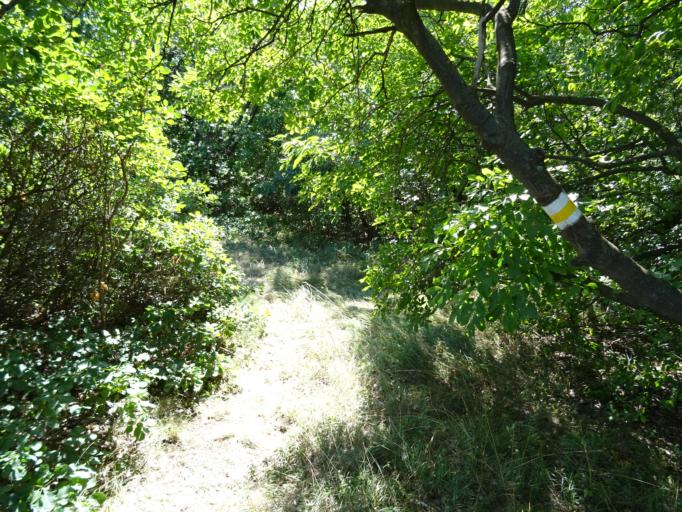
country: HU
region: Veszprem
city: Petfuerdo
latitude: 47.1666
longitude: 18.1136
